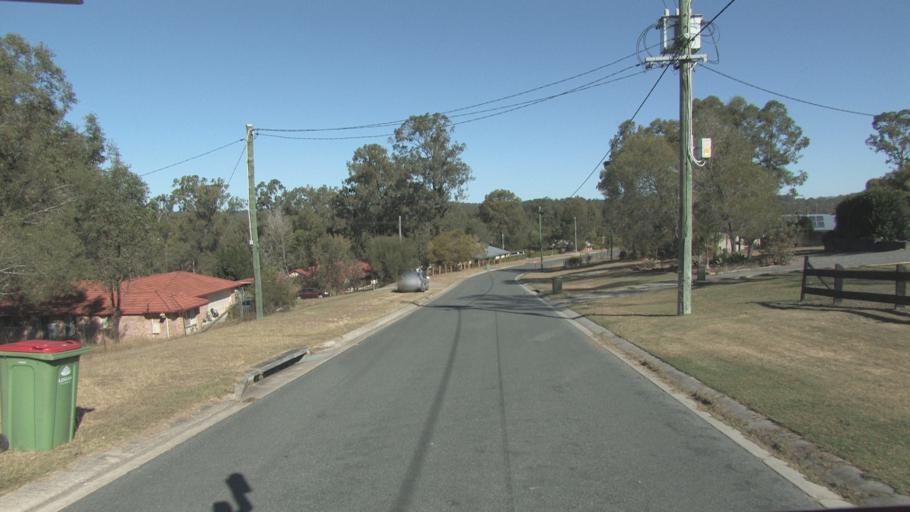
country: AU
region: Queensland
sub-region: Logan
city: Cedar Vale
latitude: -27.8551
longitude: 153.0122
